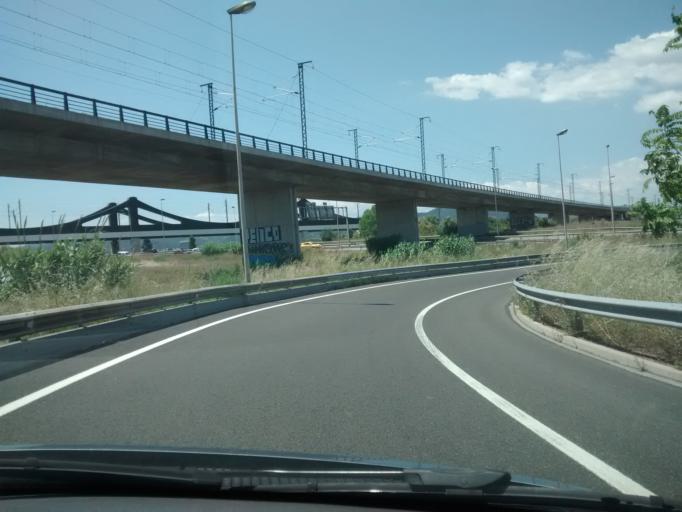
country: ES
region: Catalonia
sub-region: Provincia de Barcelona
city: Sant Joan Despi
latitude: 41.3515
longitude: 2.0561
